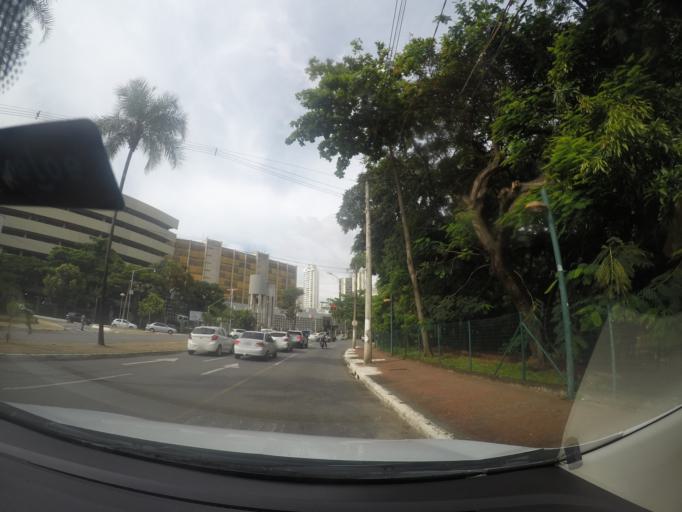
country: BR
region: Goias
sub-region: Goiania
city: Goiania
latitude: -16.6833
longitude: -49.2602
